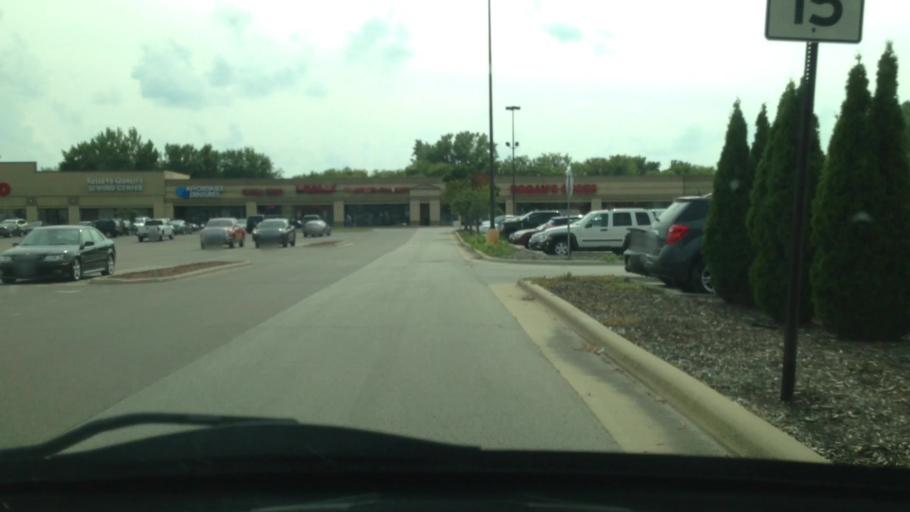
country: US
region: Minnesota
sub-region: Olmsted County
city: Rochester
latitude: 44.0775
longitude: -92.5140
